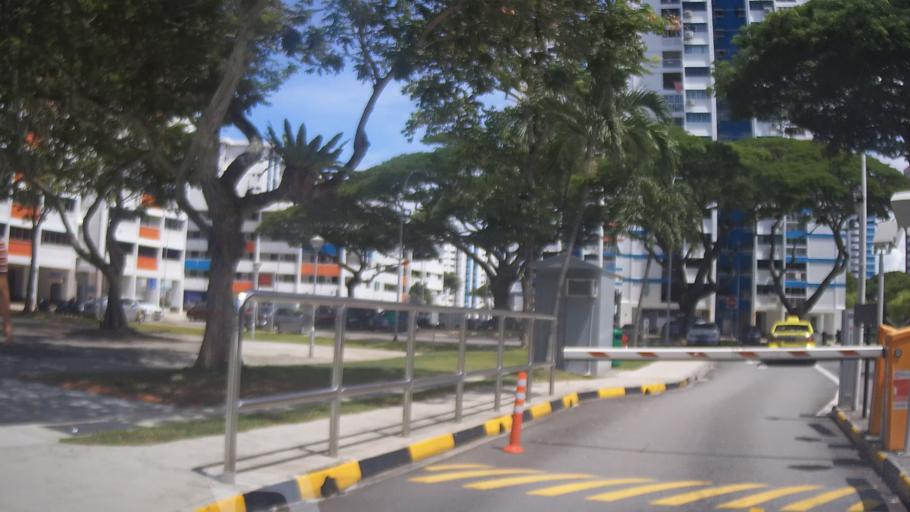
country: SG
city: Singapore
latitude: 1.3230
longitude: 103.8842
